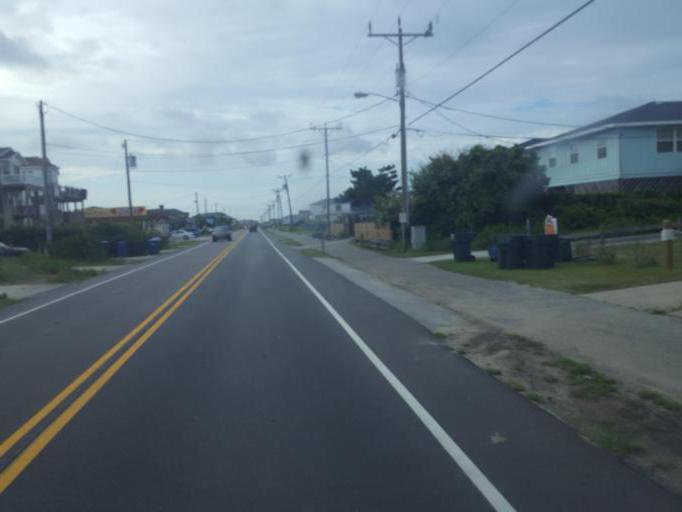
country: US
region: North Carolina
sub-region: Dare County
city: Nags Head
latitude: 35.9164
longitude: -75.6012
